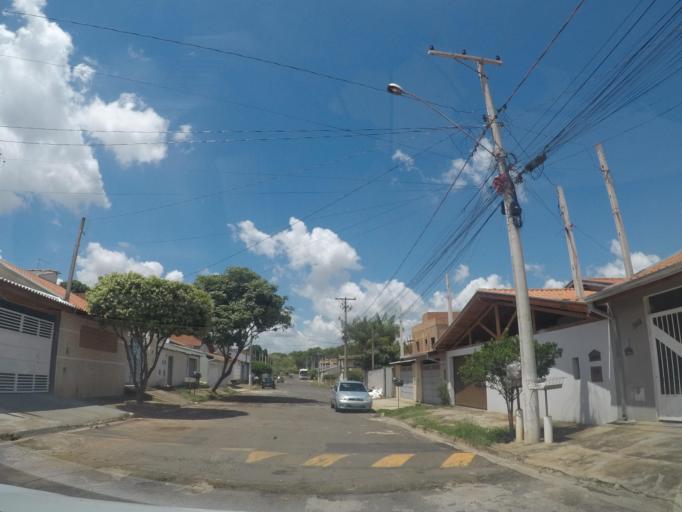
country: BR
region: Sao Paulo
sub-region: Hortolandia
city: Hortolandia
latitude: -22.8276
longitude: -47.2029
